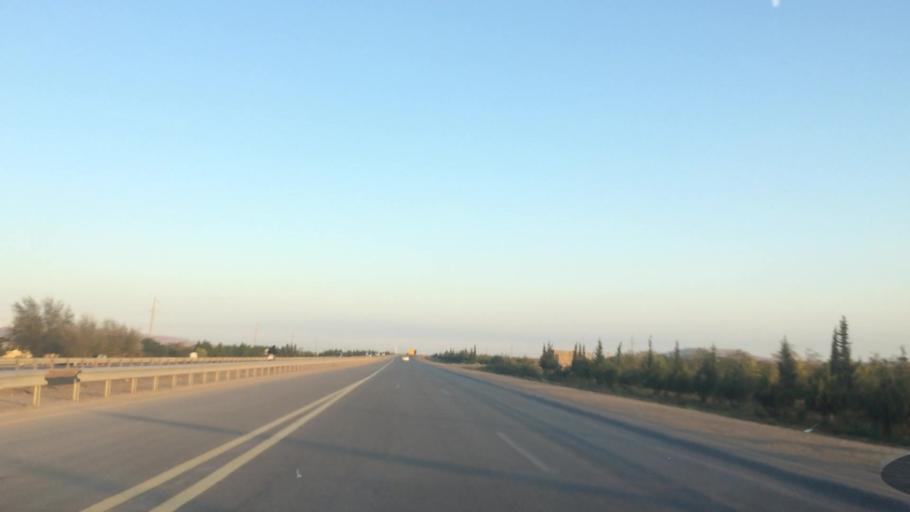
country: AZ
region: Haciqabul
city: Haciqabul
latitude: 40.0061
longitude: 49.1599
